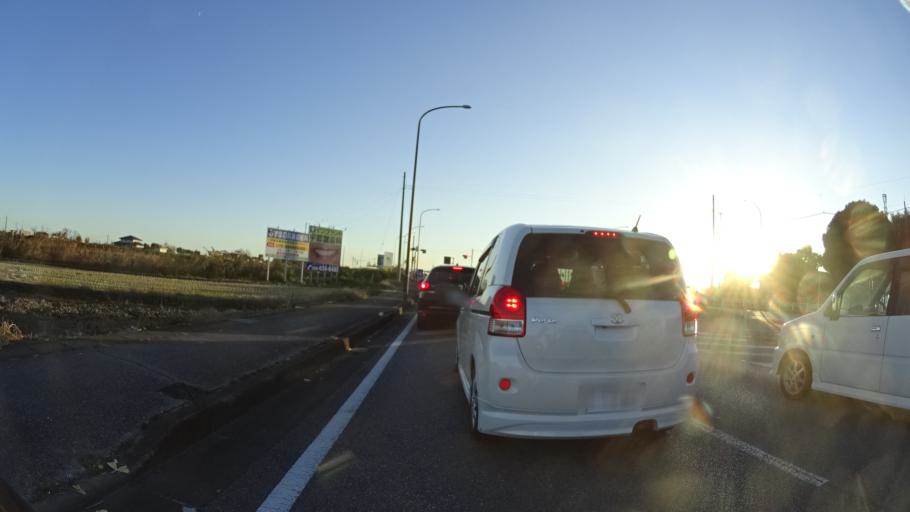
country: JP
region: Tochigi
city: Utsunomiya-shi
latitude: 36.5220
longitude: 139.8413
